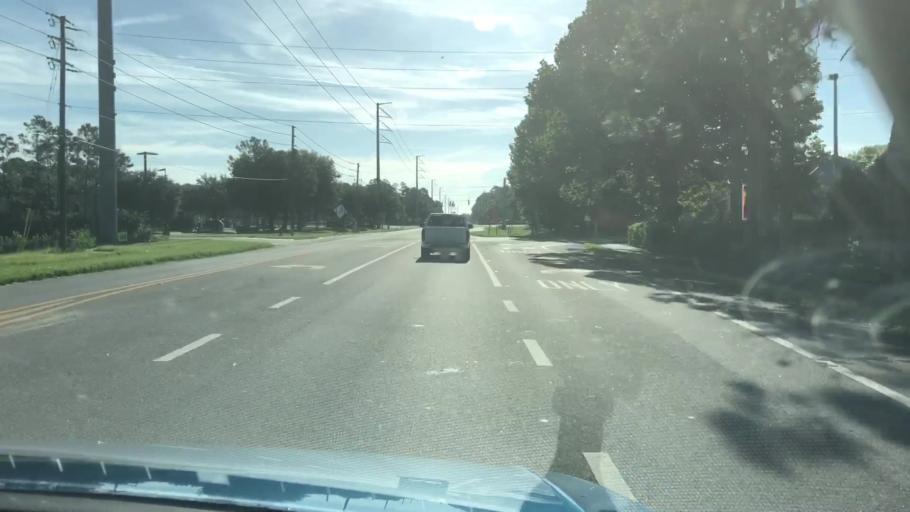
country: US
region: Florida
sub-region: Lake County
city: Eustis
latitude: 28.8752
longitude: -81.6902
